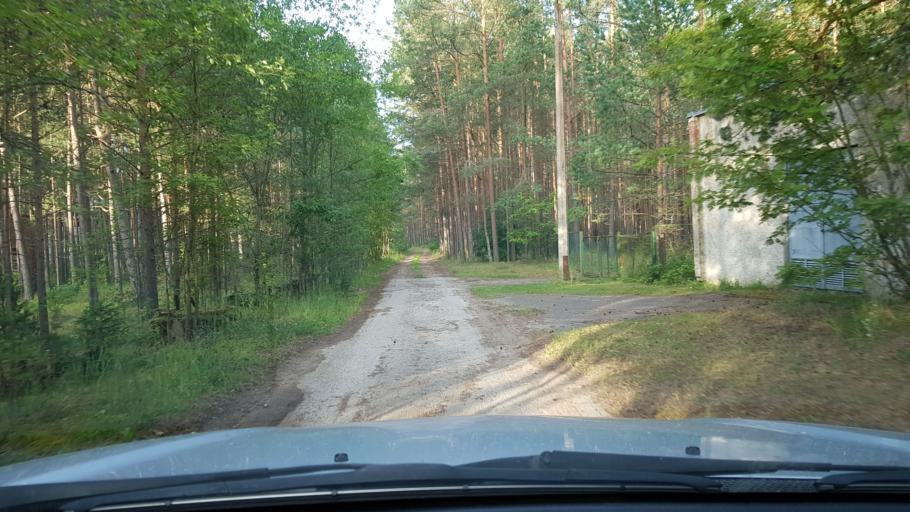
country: EE
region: Ida-Virumaa
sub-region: Narva-Joesuu linn
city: Narva-Joesuu
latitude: 59.4540
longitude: 28.0454
